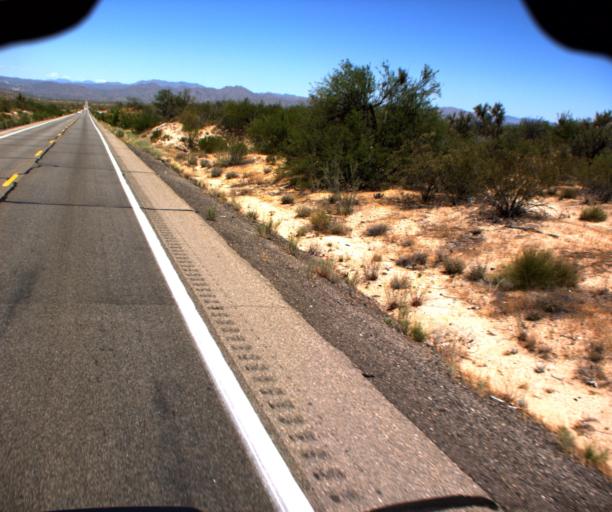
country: US
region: Arizona
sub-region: Yavapai County
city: Bagdad
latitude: 34.3052
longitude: -113.1224
